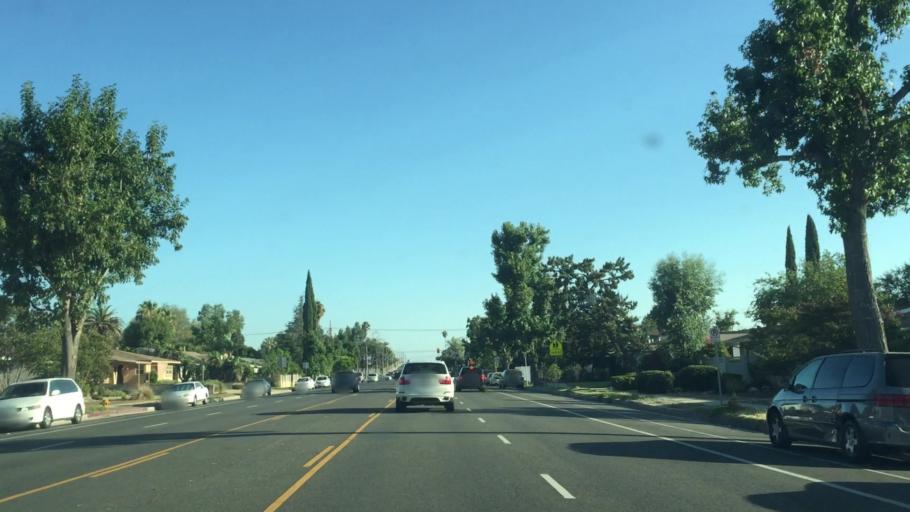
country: US
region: California
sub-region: Los Angeles County
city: San Fernando
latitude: 34.2522
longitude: -118.4850
